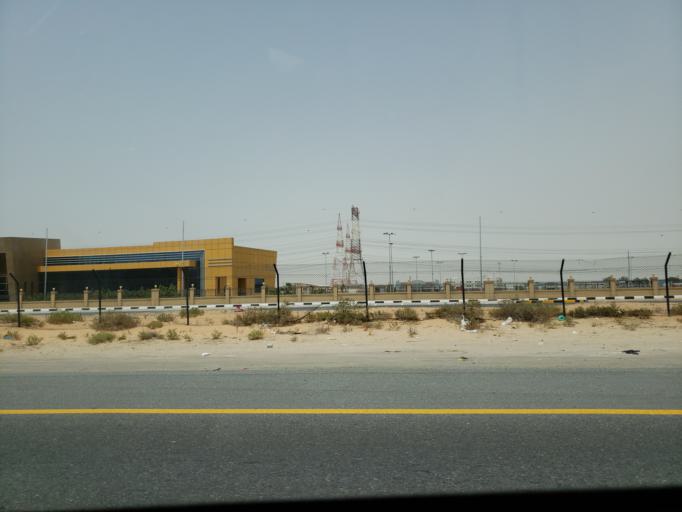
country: AE
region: Ajman
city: Ajman
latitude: 25.3647
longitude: 55.4714
